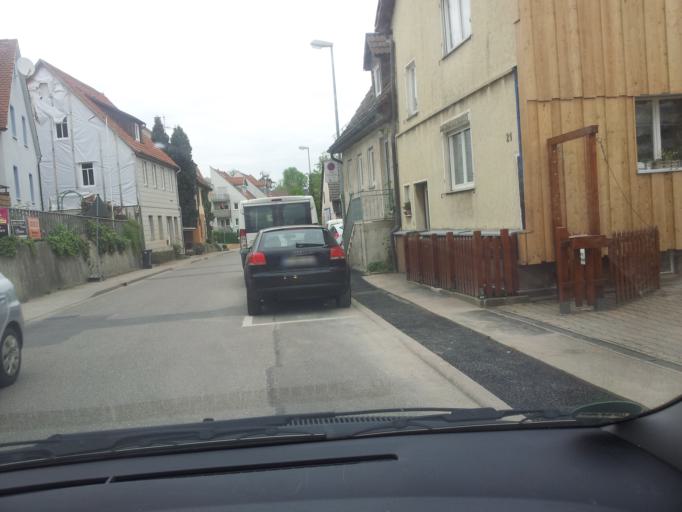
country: DE
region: Baden-Wuerttemberg
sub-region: Regierungsbezirk Stuttgart
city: Weinstadt-Endersbach
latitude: 48.7887
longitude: 9.3386
